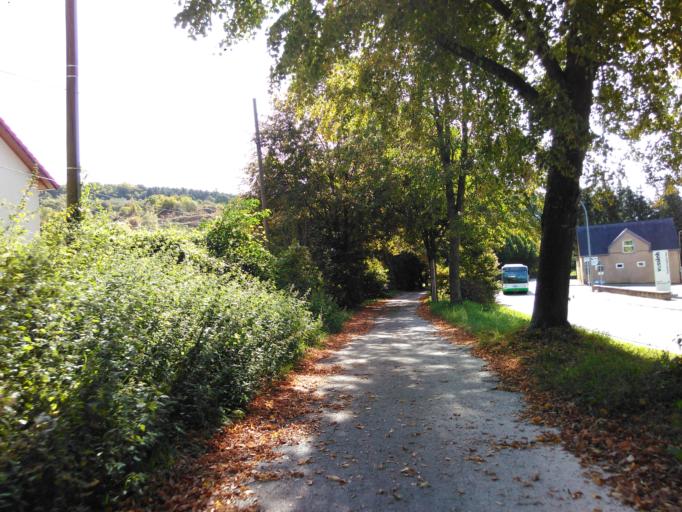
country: LU
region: Luxembourg
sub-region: Canton d'Esch-sur-Alzette
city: Rumelange
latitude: 49.4654
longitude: 6.0369
